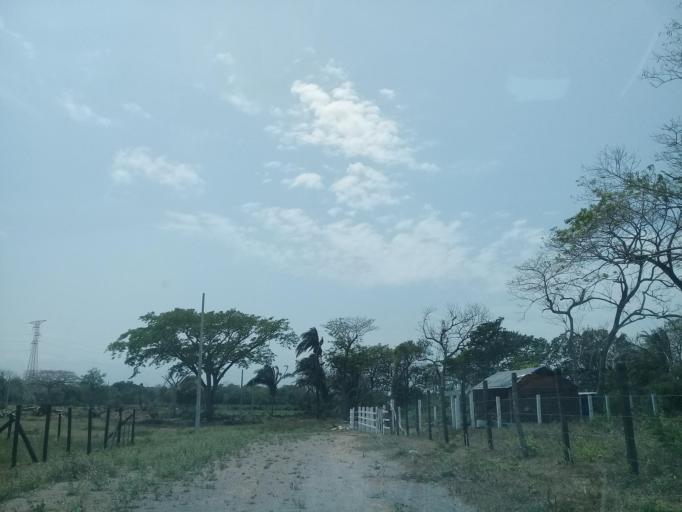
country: MX
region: Veracruz
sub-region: Veracruz
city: Delfino Victoria (Santa Fe)
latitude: 19.1747
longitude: -96.2812
